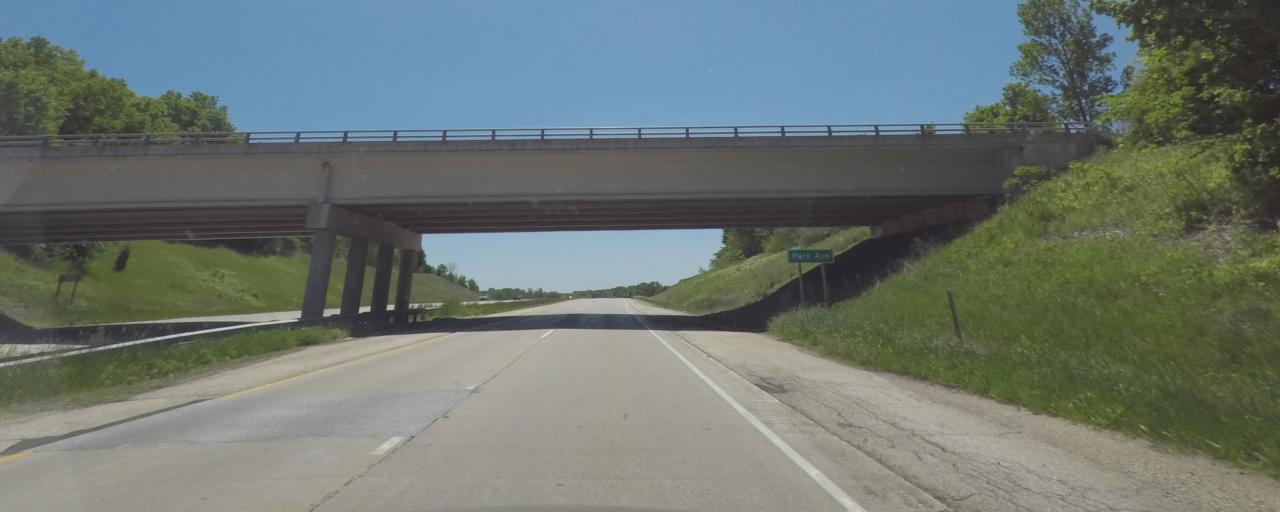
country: US
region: Wisconsin
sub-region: Washington County
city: West Bend
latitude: 43.4328
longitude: -88.2091
